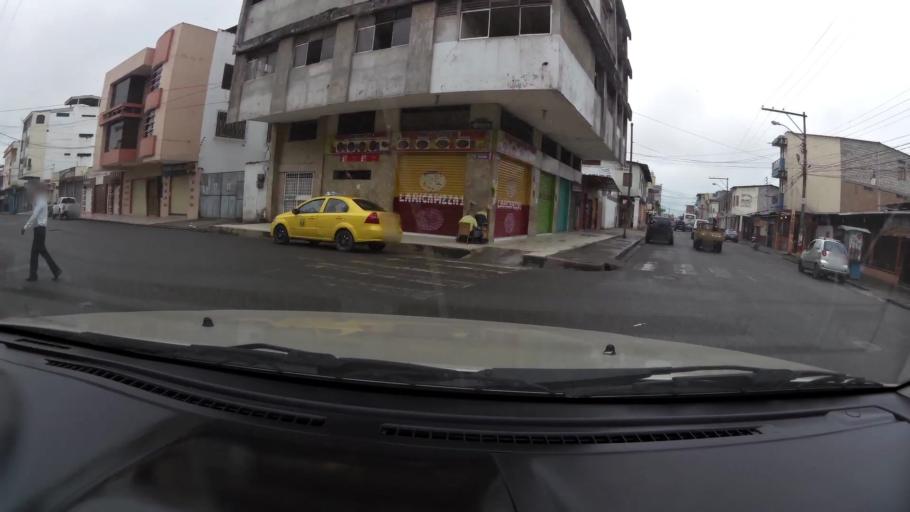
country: EC
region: El Oro
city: Pasaje
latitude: -3.3285
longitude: -79.8093
